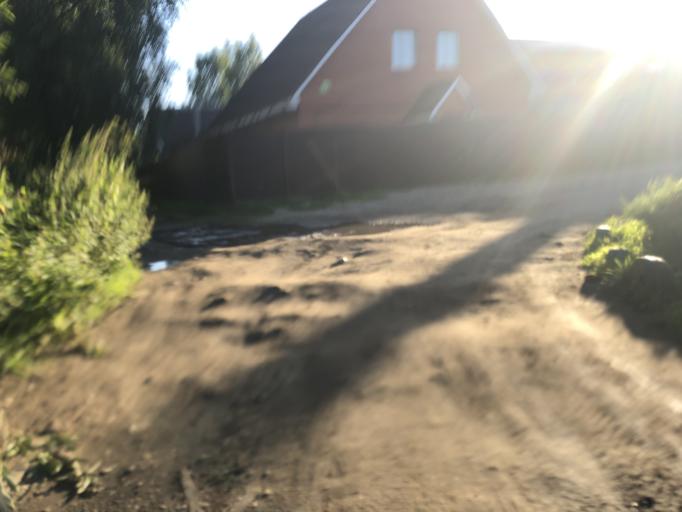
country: RU
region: Tverskaya
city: Rzhev
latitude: 56.2432
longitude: 34.3118
